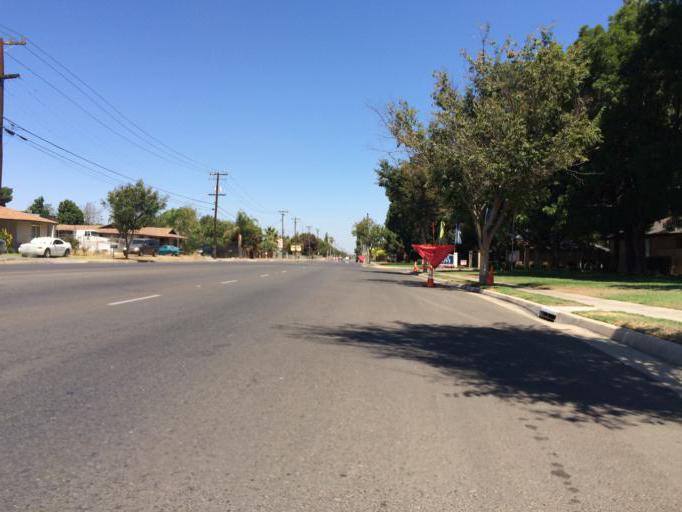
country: US
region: California
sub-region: Fresno County
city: Fresno
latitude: 36.7182
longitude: -119.7456
